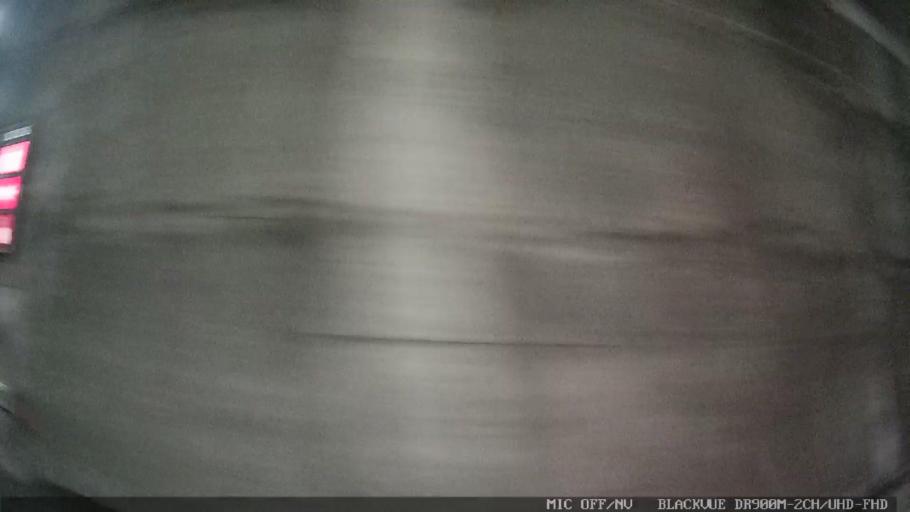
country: BR
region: Sao Paulo
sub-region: Cubatao
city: Cubatao
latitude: -23.8908
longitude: -46.5058
